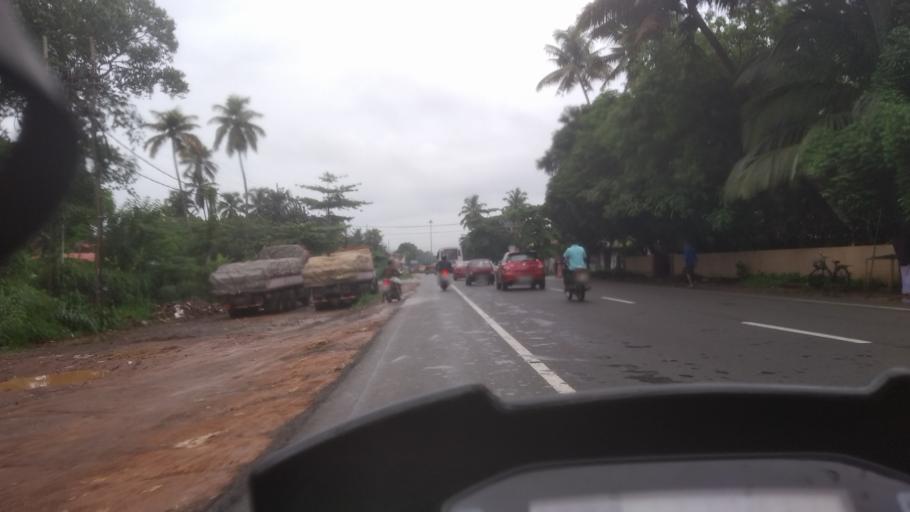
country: IN
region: Kerala
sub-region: Alappuzha
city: Kayankulam
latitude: 9.1688
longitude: 76.4996
